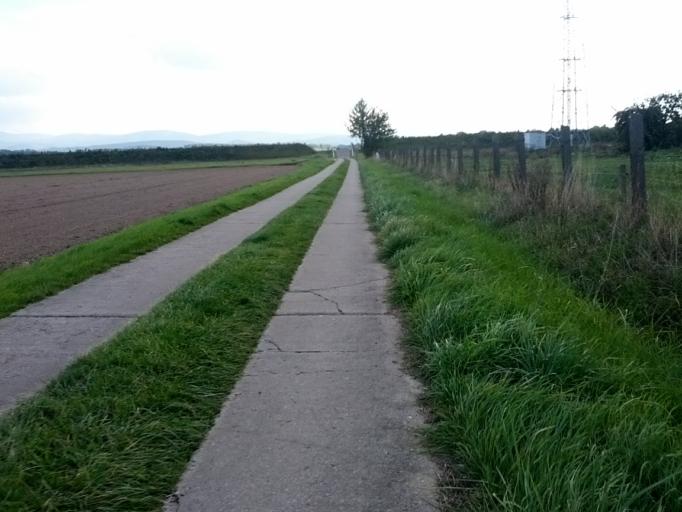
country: DE
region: Thuringia
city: Eisenach
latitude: 51.0169
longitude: 10.3379
